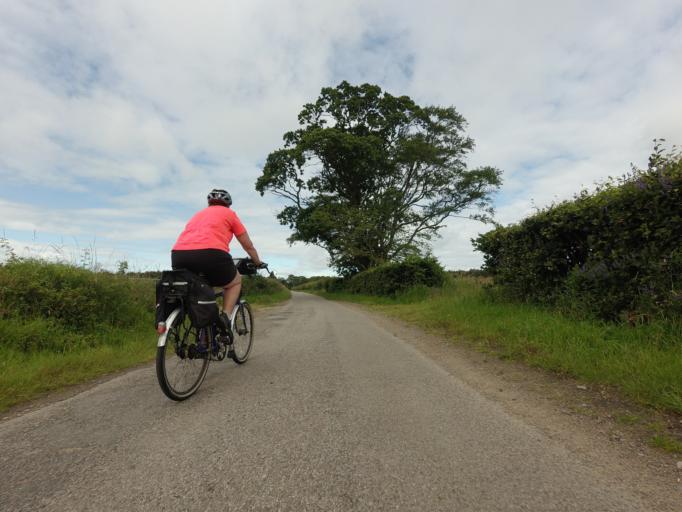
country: GB
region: Scotland
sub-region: Moray
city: Hopeman
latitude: 57.6701
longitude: -3.3908
